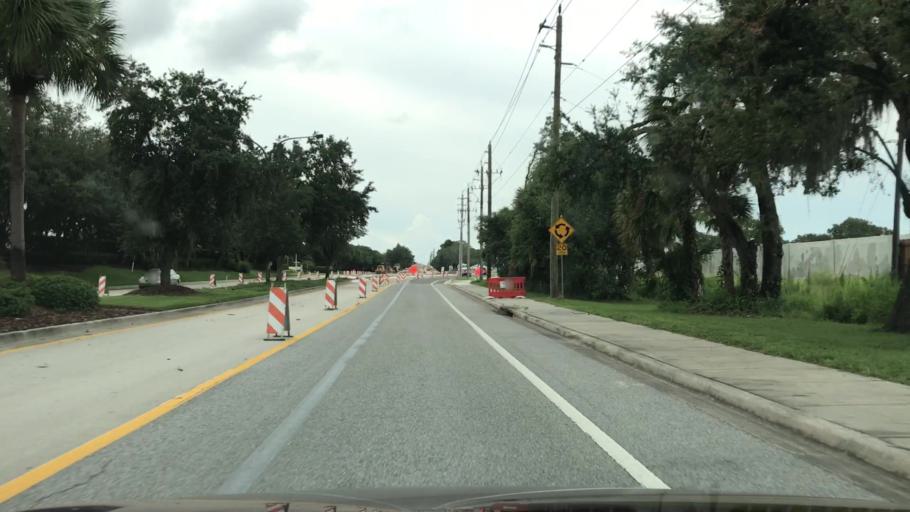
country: US
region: Florida
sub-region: Sarasota County
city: Bee Ridge
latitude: 27.2523
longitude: -82.4647
